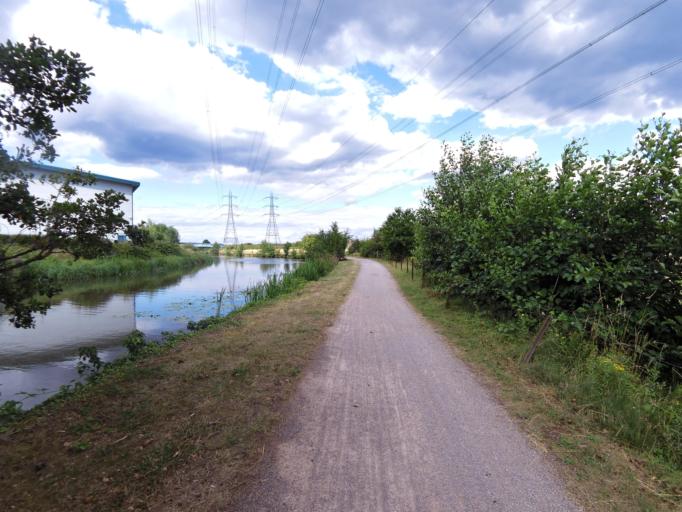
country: GB
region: England
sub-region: Hertfordshire
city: Waltham Cross
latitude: 51.6496
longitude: -0.0229
